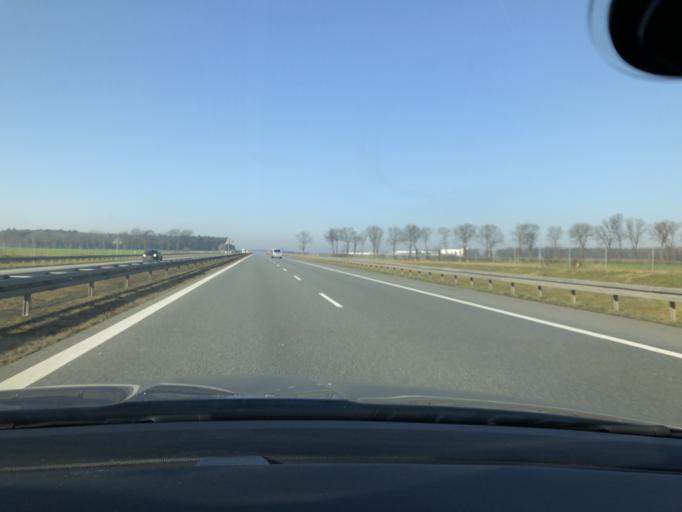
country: PL
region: Greater Poland Voivodeship
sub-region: Powiat poznanski
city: Dopiewo
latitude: 52.3596
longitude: 16.6120
